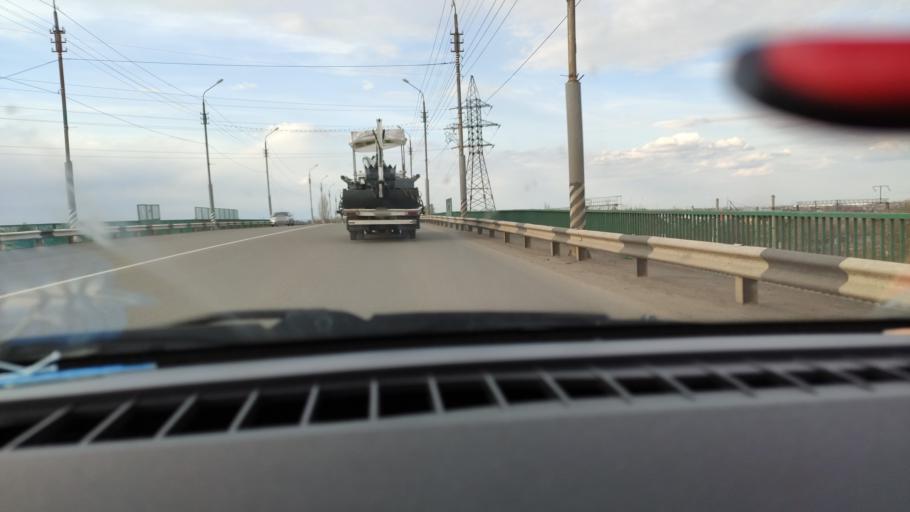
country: RU
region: Saratov
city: Privolzhskiy
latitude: 51.4179
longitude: 46.0454
